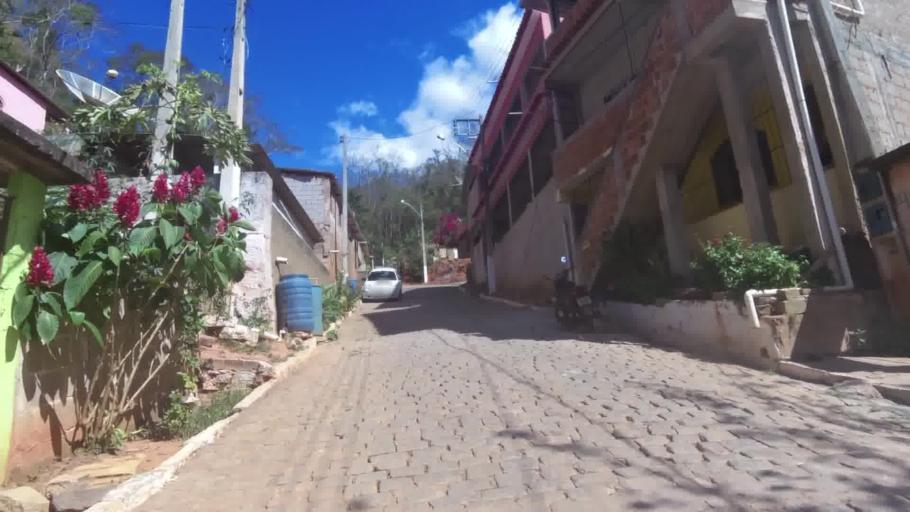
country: BR
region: Espirito Santo
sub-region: Cachoeiro De Itapemirim
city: Cachoeiro de Itapemirim
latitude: -20.9187
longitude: -41.1975
